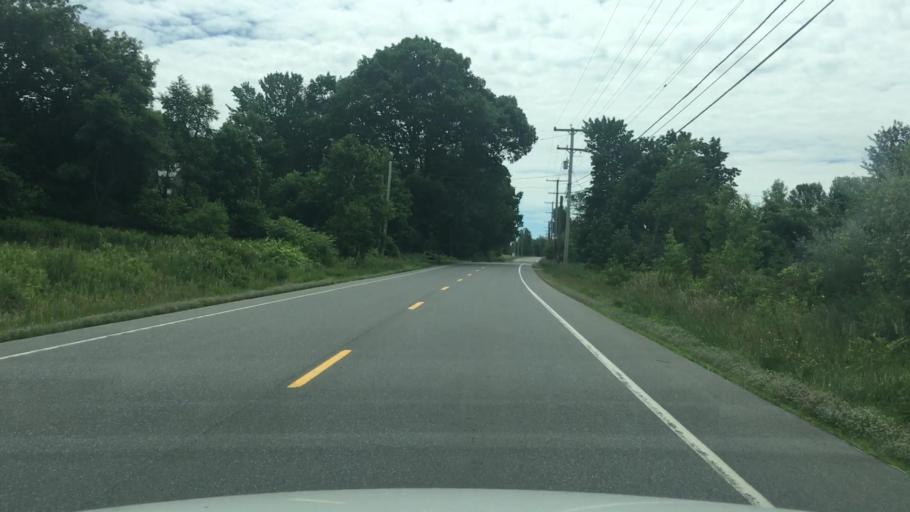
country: US
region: Maine
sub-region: Waldo County
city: Troy
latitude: 44.5662
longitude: -69.2766
